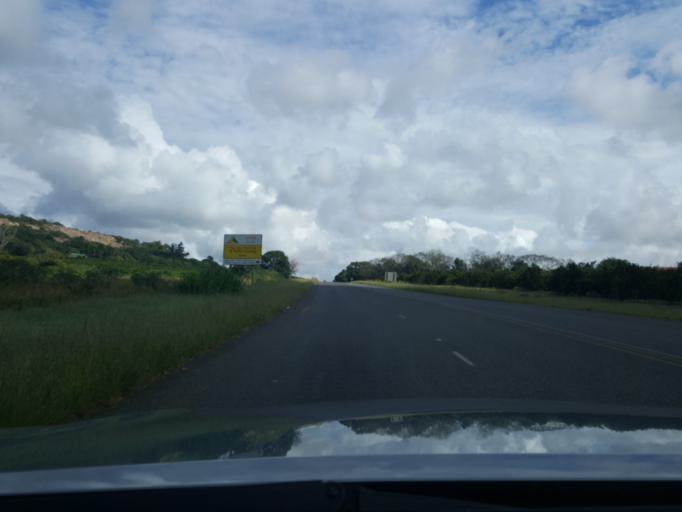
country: ZA
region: Mpumalanga
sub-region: Ehlanzeni District
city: Nelspruit
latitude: -25.4699
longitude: 31.0533
